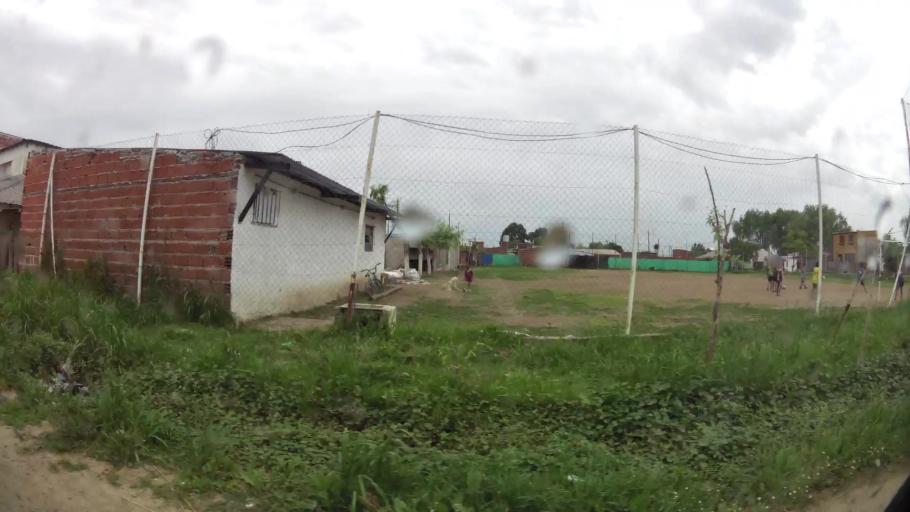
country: AR
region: Buenos Aires
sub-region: Partido de Zarate
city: Zarate
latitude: -34.1102
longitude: -59.0422
